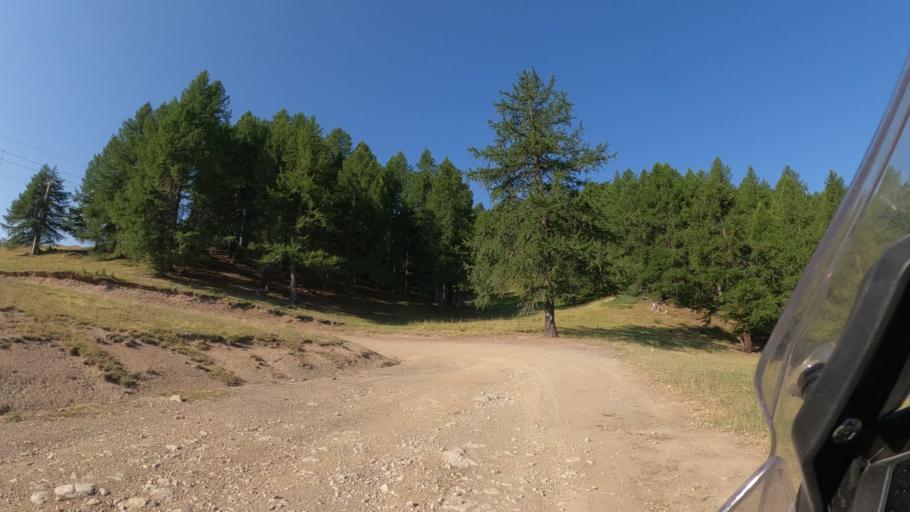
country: FR
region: Provence-Alpes-Cote d'Azur
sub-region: Departement des Hautes-Alpes
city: Guillestre
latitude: 44.6151
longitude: 6.6241
